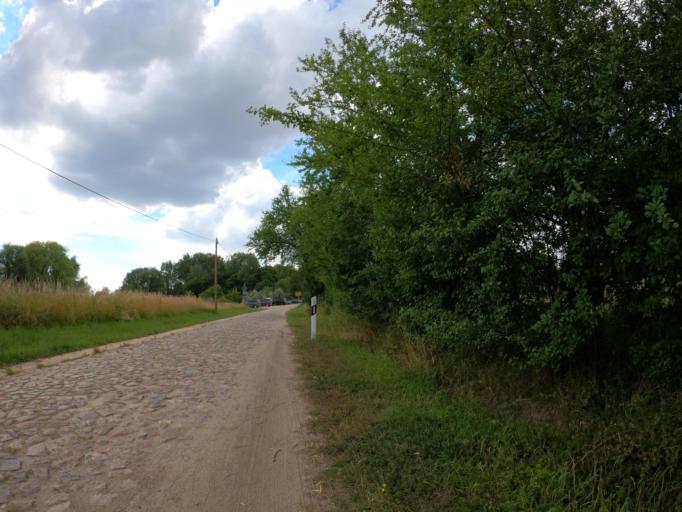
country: DE
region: Mecklenburg-Vorpommern
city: Woldegk
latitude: 53.4137
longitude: 13.6182
